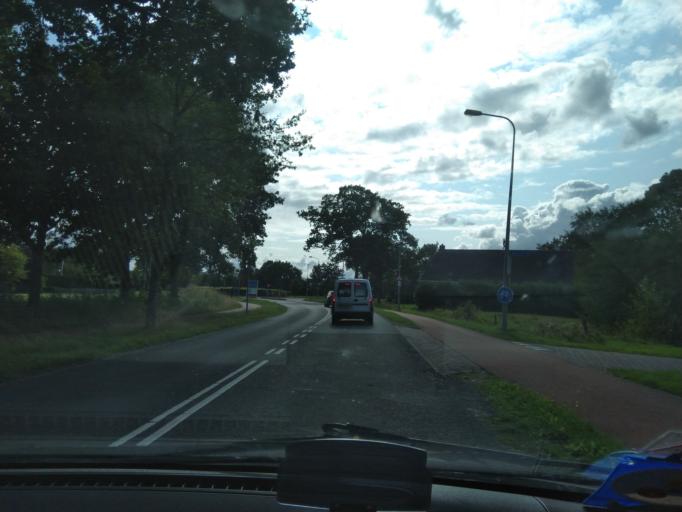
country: NL
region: Groningen
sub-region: Gemeente Groningen
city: Groningen
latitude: 53.1793
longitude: 6.5438
